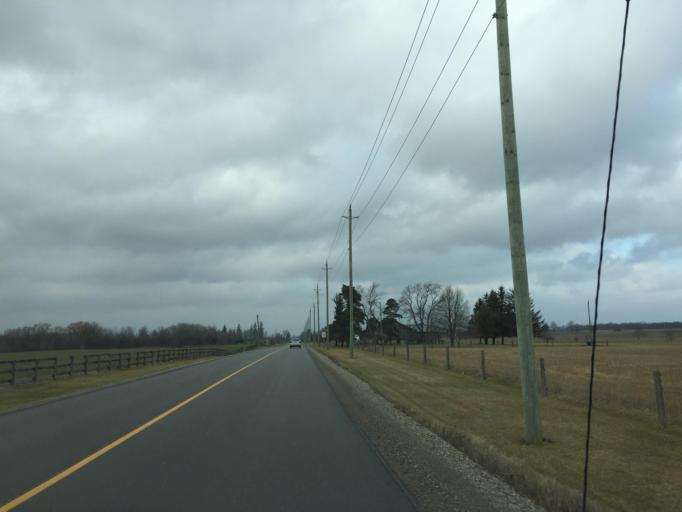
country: CA
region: Ontario
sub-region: Wellington County
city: Guelph
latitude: 43.4707
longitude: -80.3305
